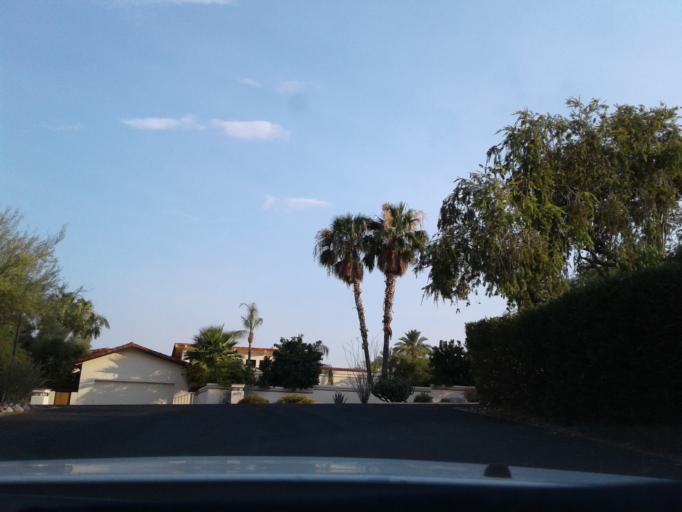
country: US
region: Arizona
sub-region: Maricopa County
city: Paradise Valley
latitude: 33.5414
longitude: -111.9790
